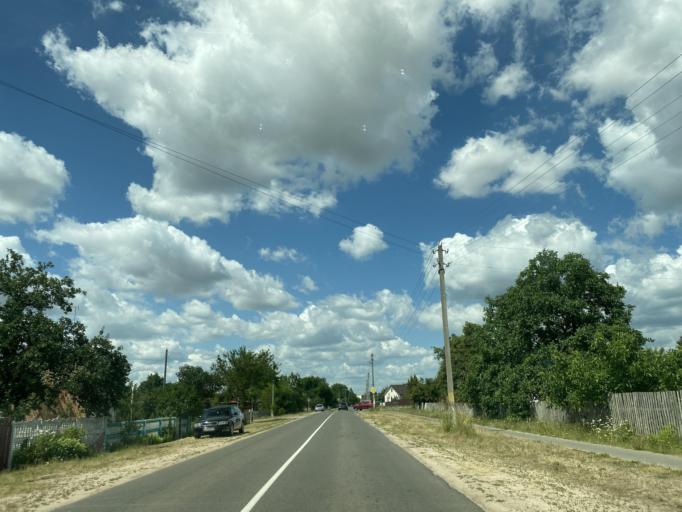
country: BY
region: Brest
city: Ivanava
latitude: 52.1417
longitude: 25.5478
